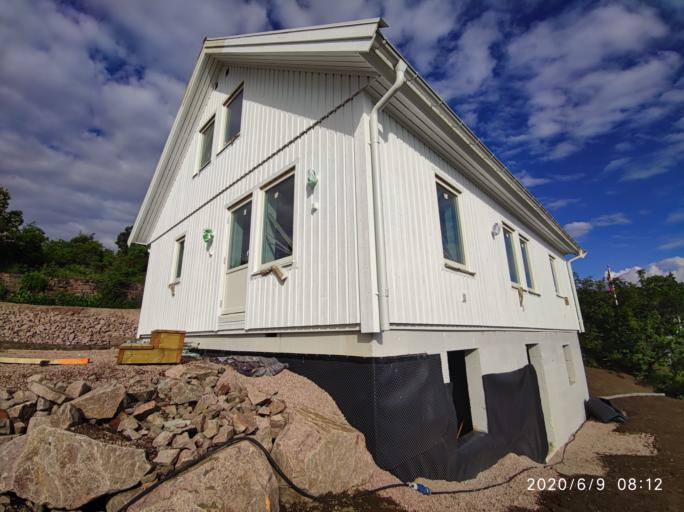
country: NO
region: Buskerud
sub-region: Hurum
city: Saetre
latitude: 59.6866
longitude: 10.5238
